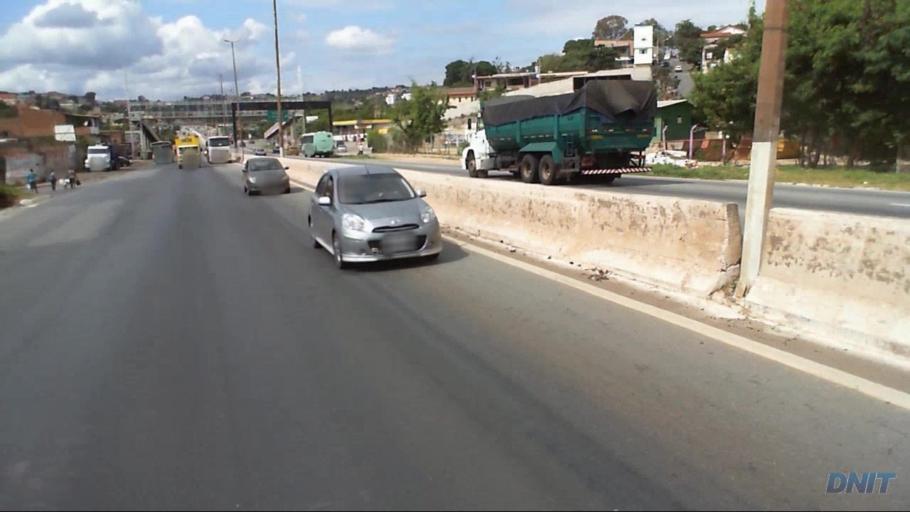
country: BR
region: Minas Gerais
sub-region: Belo Horizonte
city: Belo Horizonte
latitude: -19.8573
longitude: -43.9026
